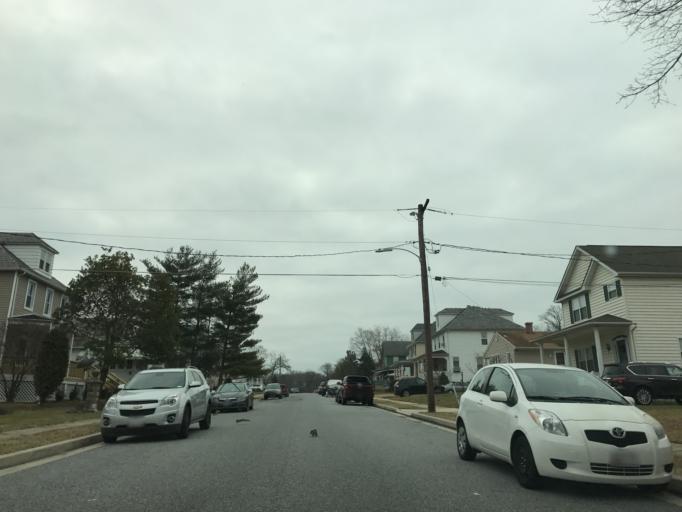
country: US
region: Maryland
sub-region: Baltimore County
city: Overlea
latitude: 39.3547
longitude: -76.5199
